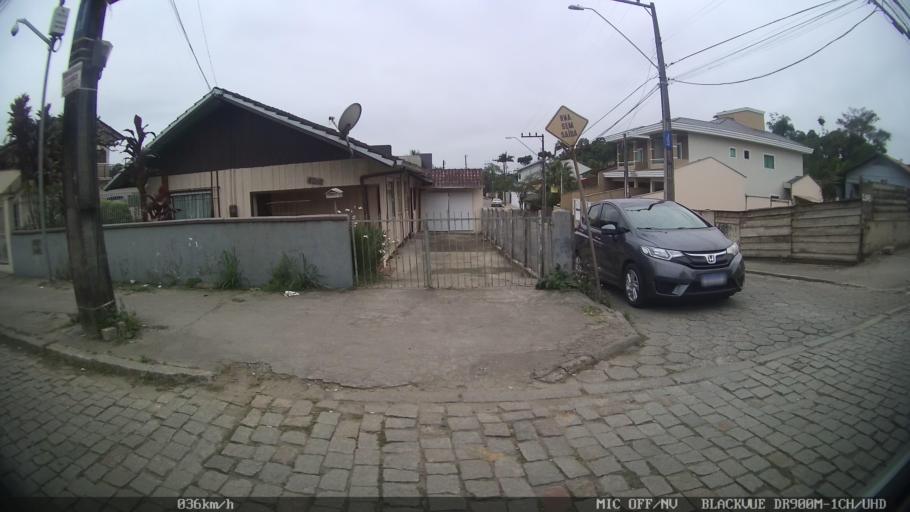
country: BR
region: Santa Catarina
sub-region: Joinville
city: Joinville
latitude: -26.3328
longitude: -48.8578
